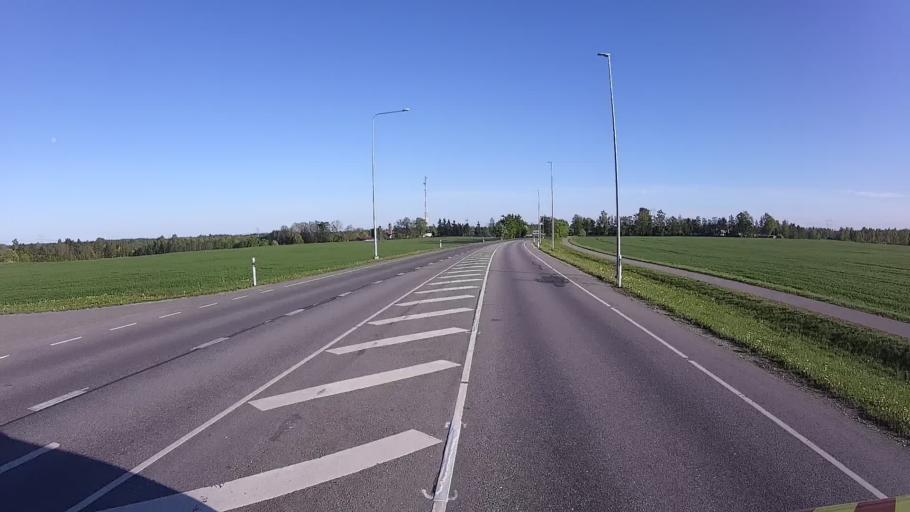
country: EE
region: Viljandimaa
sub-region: Viljandi linn
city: Viljandi
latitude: 58.3894
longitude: 25.5944
